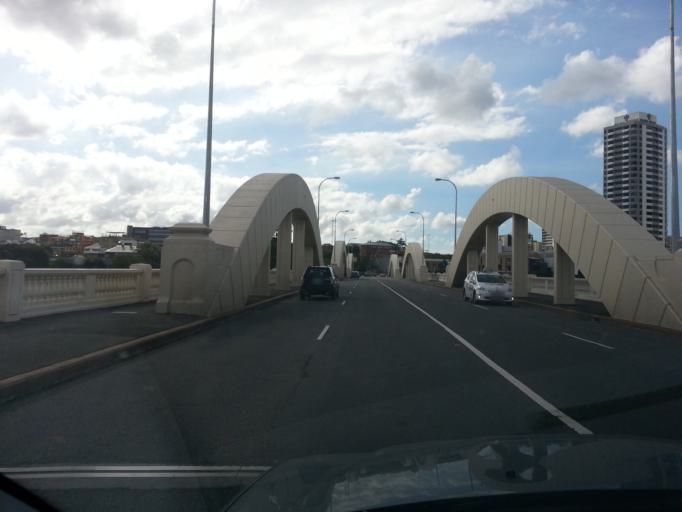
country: AU
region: Queensland
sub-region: Brisbane
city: Spring Hill
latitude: -27.4695
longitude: 153.0158
